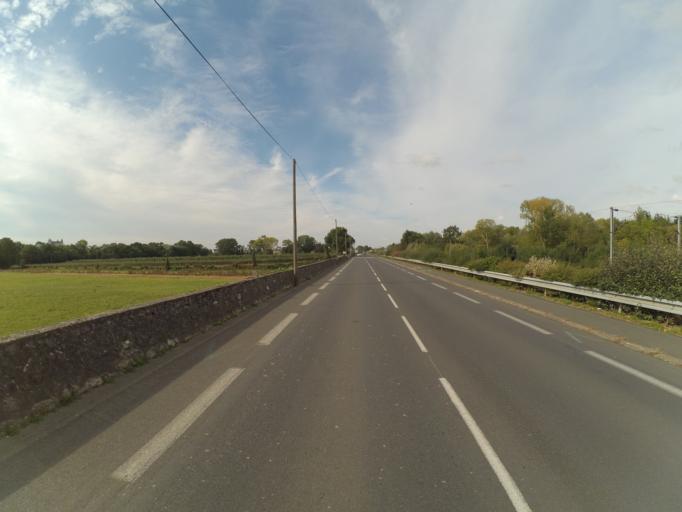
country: FR
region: Pays de la Loire
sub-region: Departement de Maine-et-Loire
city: Saumur
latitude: 47.2642
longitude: -0.0598
